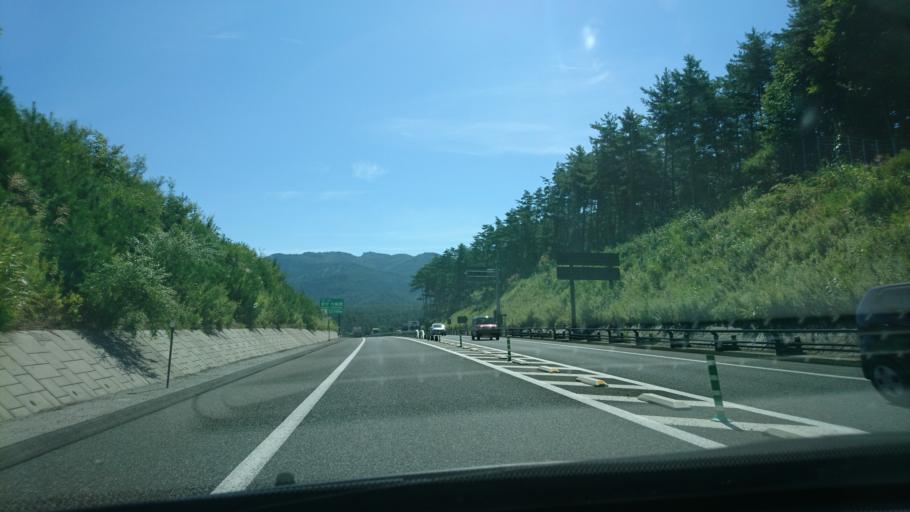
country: JP
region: Iwate
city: Tono
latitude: 39.2941
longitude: 141.3929
